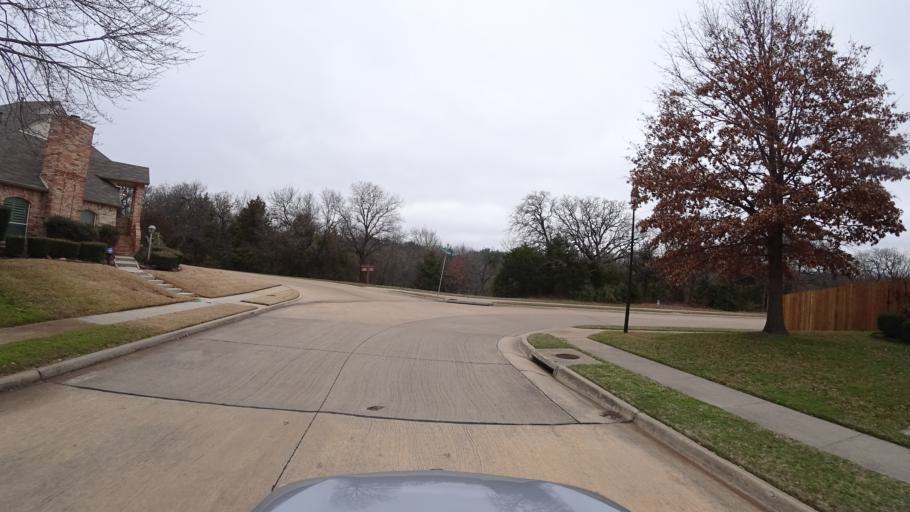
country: US
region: Texas
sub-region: Denton County
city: Lewisville
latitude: 33.0268
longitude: -97.0342
